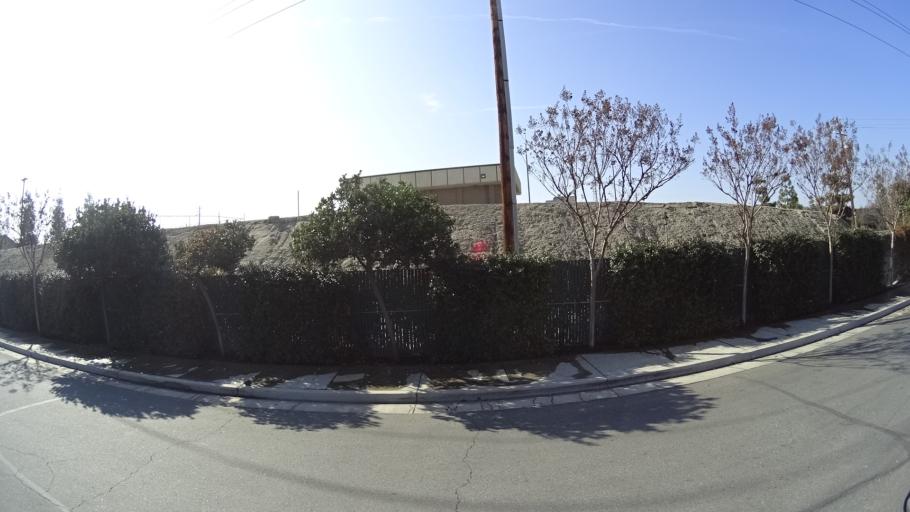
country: US
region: California
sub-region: Kern County
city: Bakersfield
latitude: 35.3791
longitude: -119.0474
